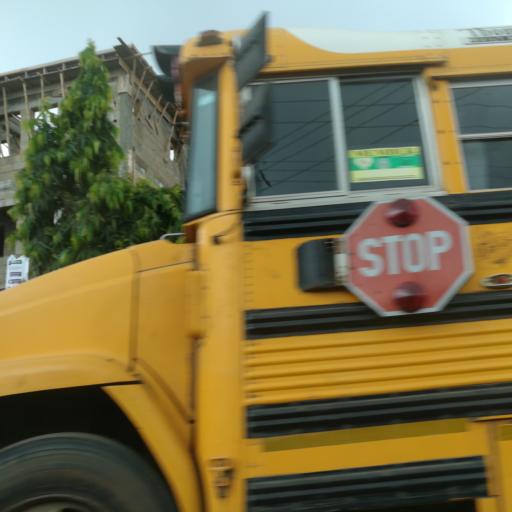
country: NG
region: Lagos
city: Agege
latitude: 6.5895
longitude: 3.3065
